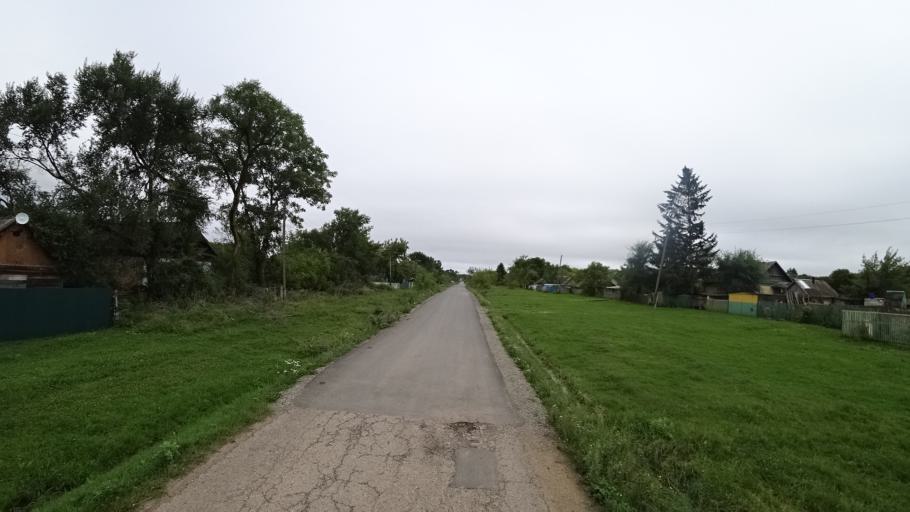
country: RU
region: Primorskiy
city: Monastyrishche
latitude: 44.0838
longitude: 132.5870
